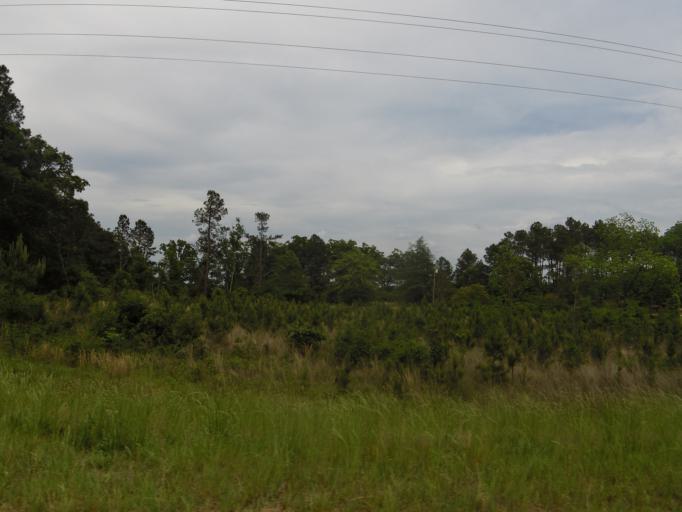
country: US
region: Georgia
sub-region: Jefferson County
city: Wrens
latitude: 33.3145
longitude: -82.4478
